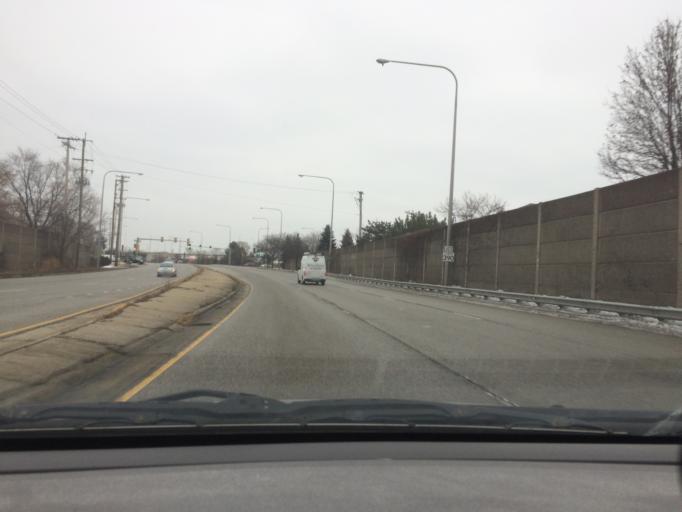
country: US
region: Illinois
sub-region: DuPage County
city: Hanover Park
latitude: 41.9985
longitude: -88.1213
